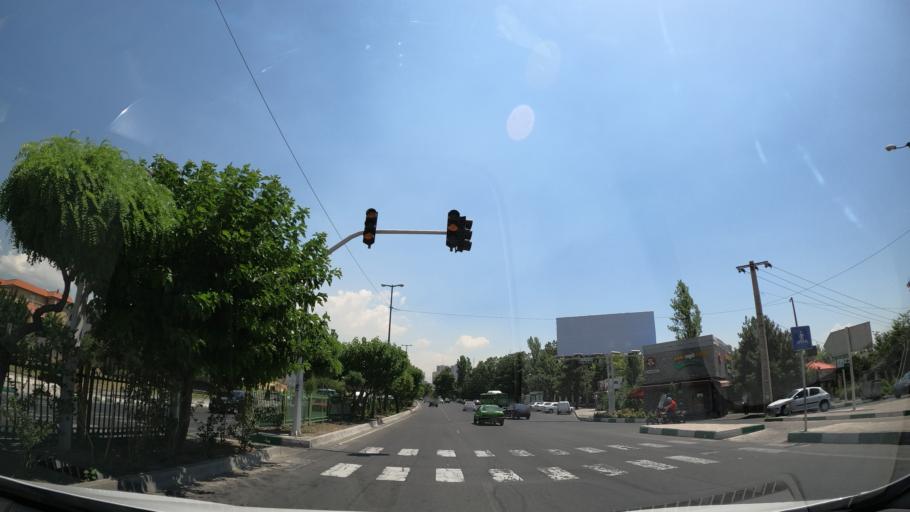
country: IR
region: Tehran
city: Tajrish
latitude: 35.7552
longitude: 51.3701
